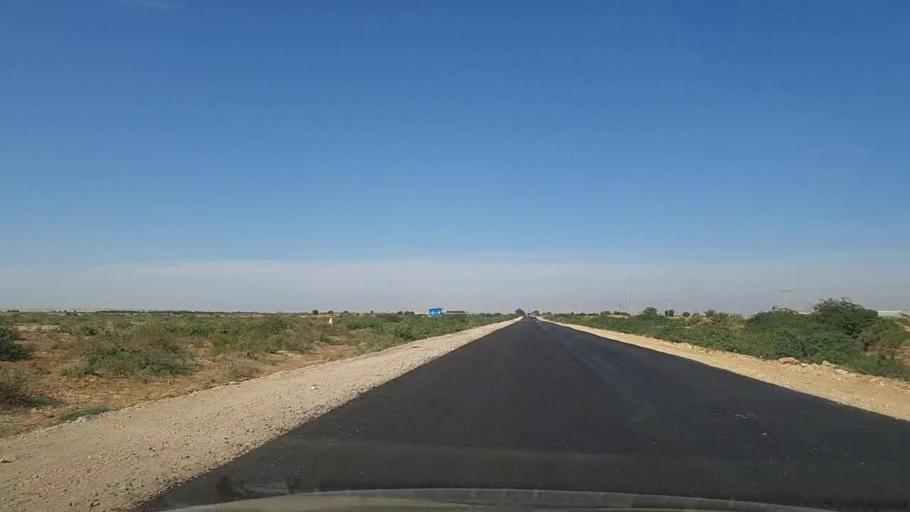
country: PK
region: Sindh
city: Kotri
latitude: 25.2398
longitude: 68.2314
